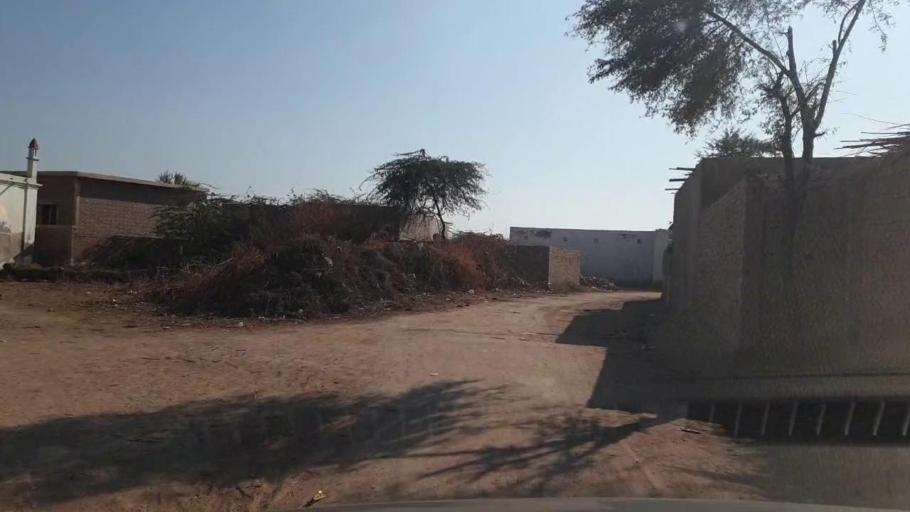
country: PK
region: Sindh
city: Shahpur Chakar
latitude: 26.1518
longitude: 68.6709
